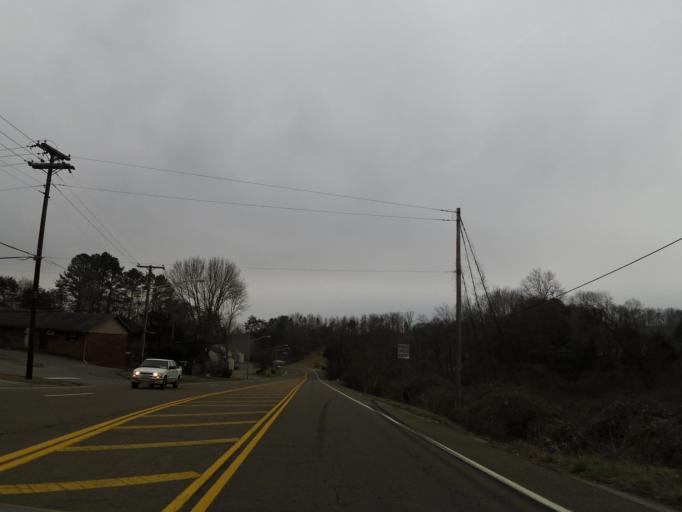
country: US
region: Tennessee
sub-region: Anderson County
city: Clinton
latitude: 36.1167
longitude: -84.1317
